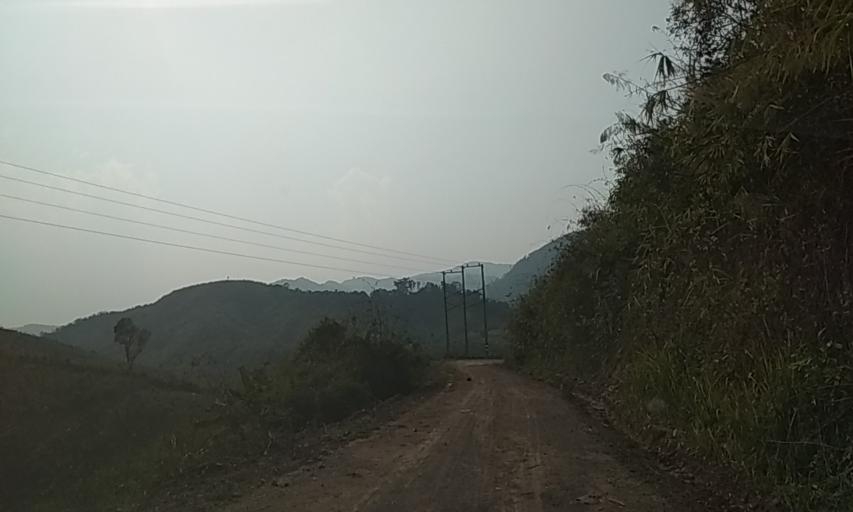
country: LA
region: Louangphabang
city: Louangphabang
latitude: 20.0402
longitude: 101.8136
